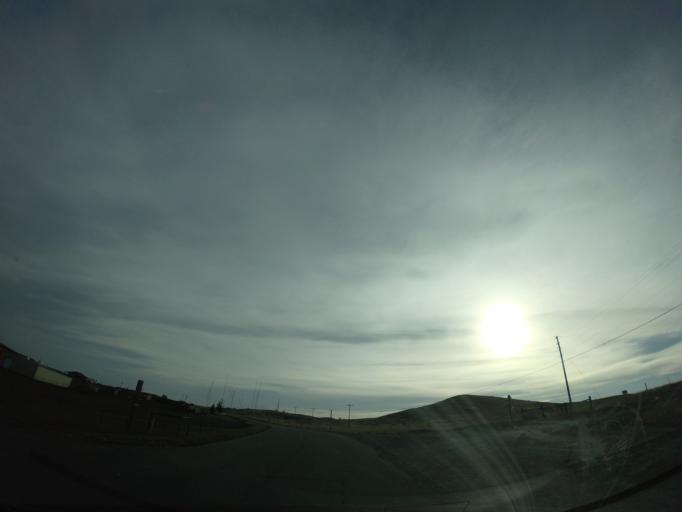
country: US
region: Montana
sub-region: Yellowstone County
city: Billings
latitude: 45.7767
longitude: -108.4627
